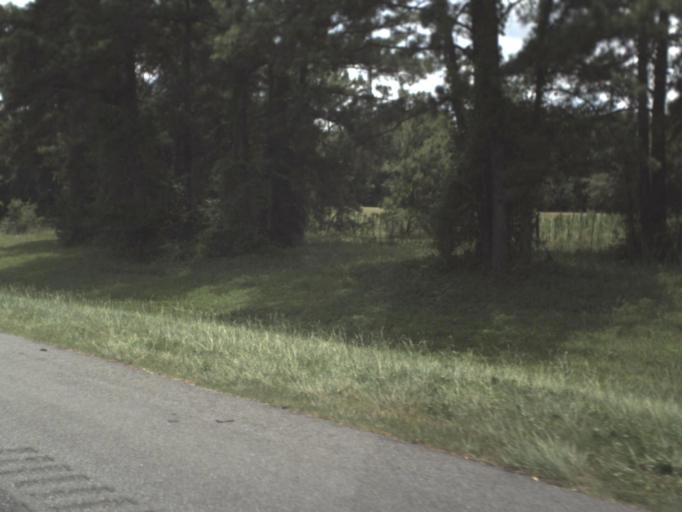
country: US
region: Florida
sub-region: Alachua County
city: High Springs
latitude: 29.9538
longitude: -82.5696
